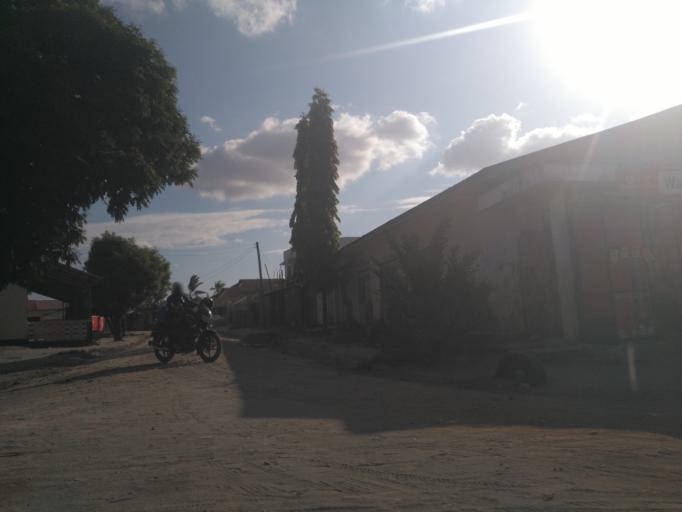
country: TZ
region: Dar es Salaam
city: Dar es Salaam
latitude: -6.8637
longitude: 39.2583
